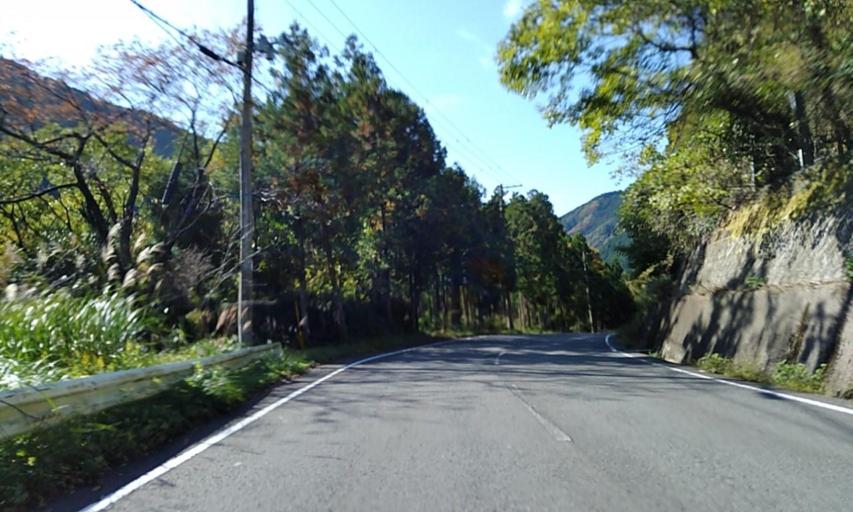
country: JP
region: Wakayama
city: Iwade
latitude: 34.0880
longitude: 135.3633
